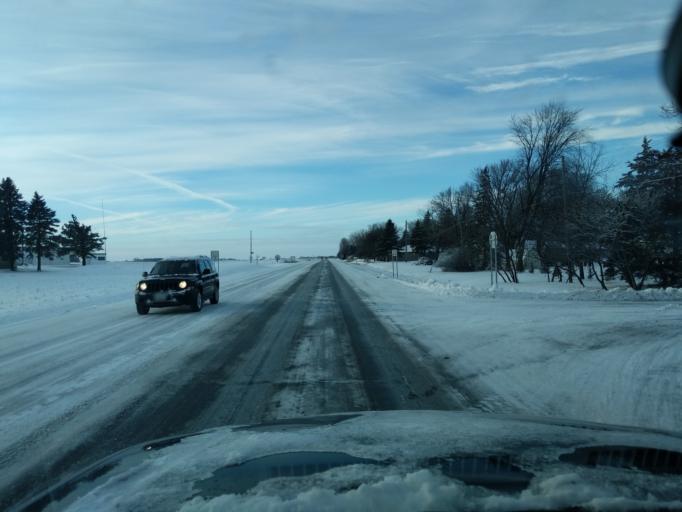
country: US
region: Minnesota
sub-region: Renville County
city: Hector
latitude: 44.7418
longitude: -94.7214
